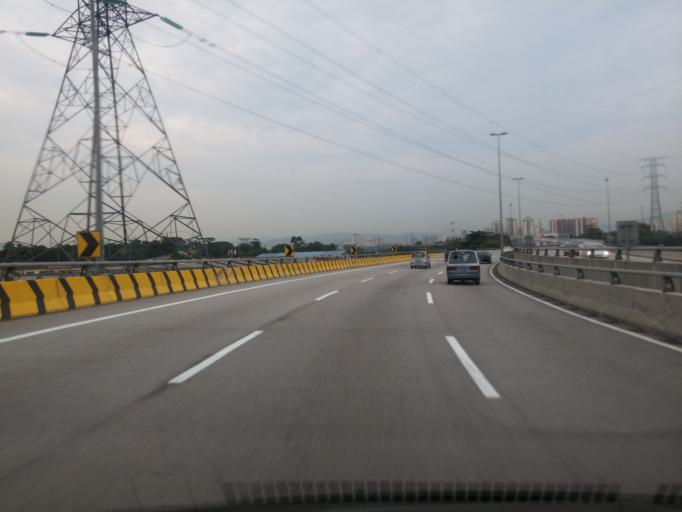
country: MY
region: Kuala Lumpur
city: Kuala Lumpur
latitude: 3.0974
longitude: 101.6964
